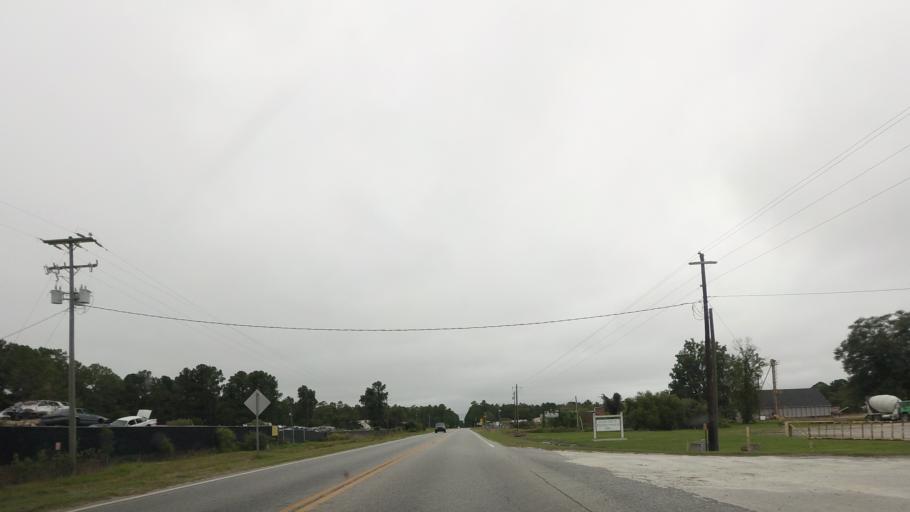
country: US
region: Georgia
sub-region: Berrien County
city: Nashville
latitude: 31.1796
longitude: -83.2371
